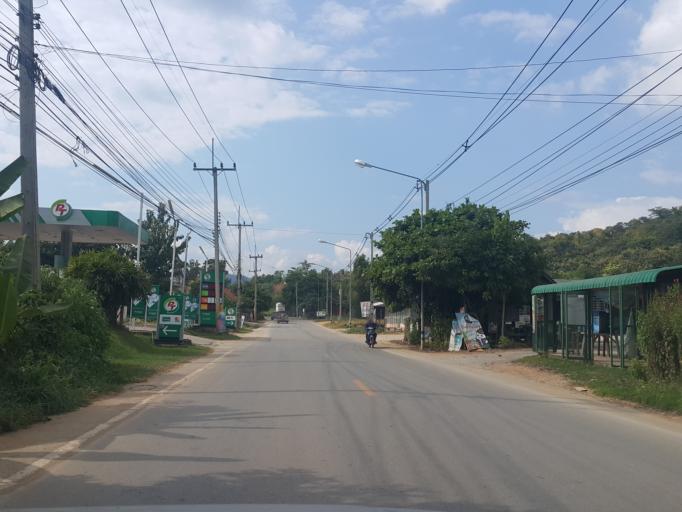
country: TH
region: Chiang Mai
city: Mae Chaem
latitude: 18.4931
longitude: 98.3757
